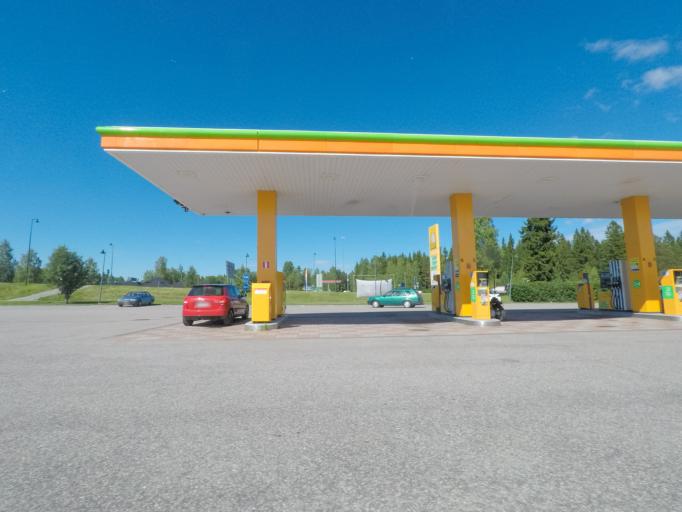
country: FI
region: Southern Savonia
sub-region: Pieksaemaeki
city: Juva
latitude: 61.8979
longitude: 27.8074
